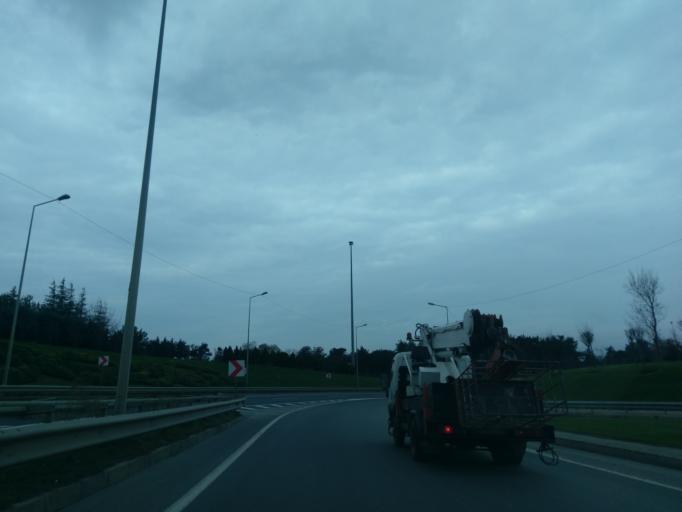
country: TR
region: Istanbul
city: Sisli
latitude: 41.1004
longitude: 28.9558
